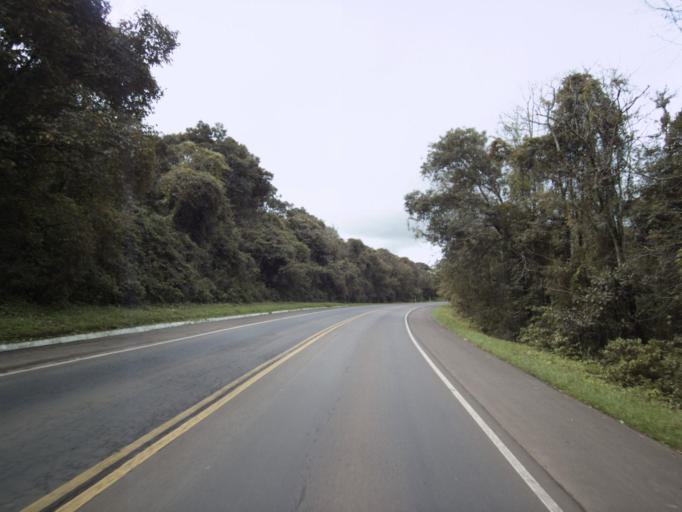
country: BR
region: Santa Catarina
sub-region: Concordia
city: Concordia
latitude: -27.2639
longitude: -51.9587
